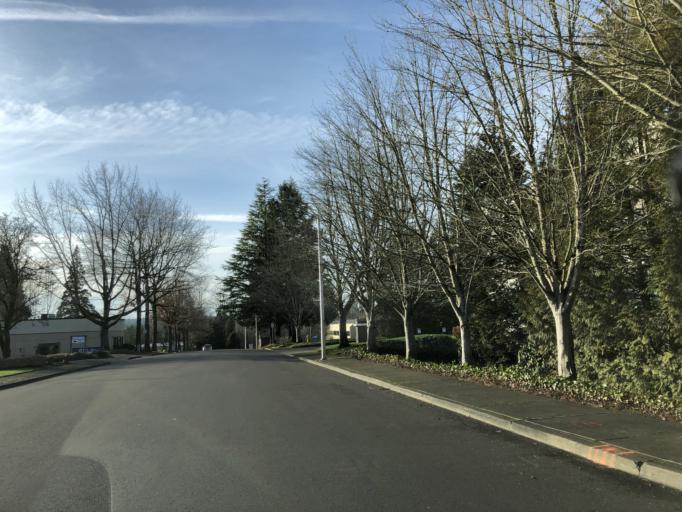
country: US
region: Oregon
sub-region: Washington County
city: Durham
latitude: 45.4215
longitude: -122.7493
